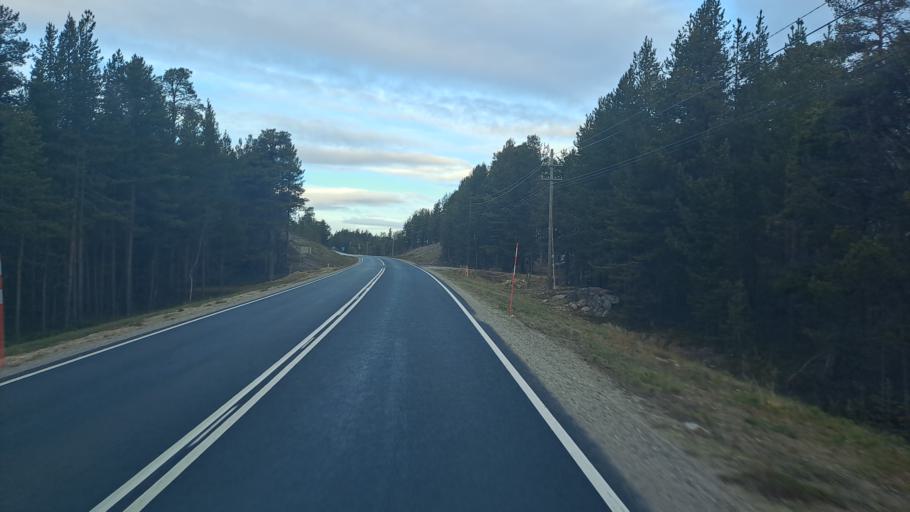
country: FI
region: Lapland
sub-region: Pohjois-Lappi
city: Inari
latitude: 68.9131
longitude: 27.0027
